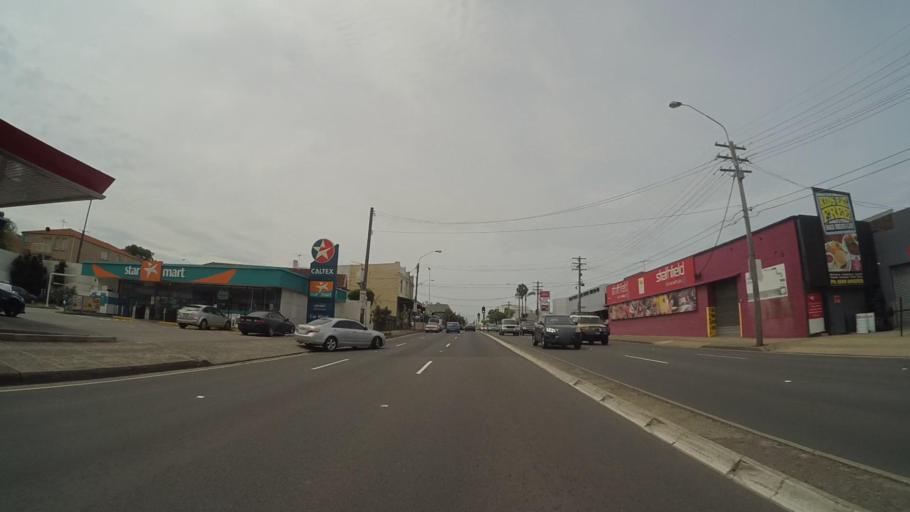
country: AU
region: New South Wales
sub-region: Rockdale
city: Arncliffe
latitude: -33.9256
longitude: 151.1598
